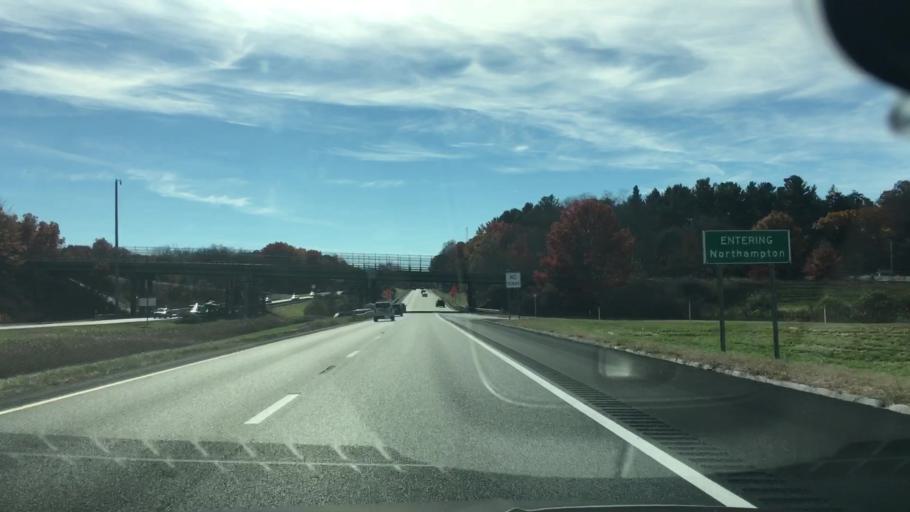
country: US
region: Massachusetts
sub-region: Hampshire County
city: Northampton
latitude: 42.3620
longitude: -72.6365
